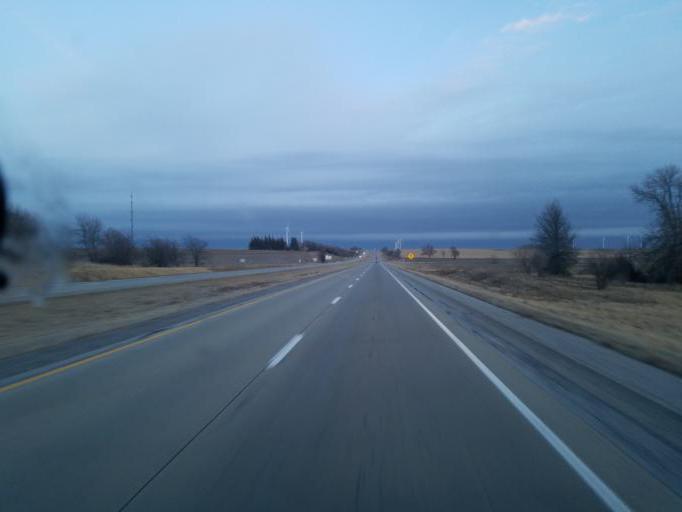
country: US
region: Iowa
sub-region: Pottawattamie County
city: Avoca
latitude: 41.4973
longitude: -95.2215
